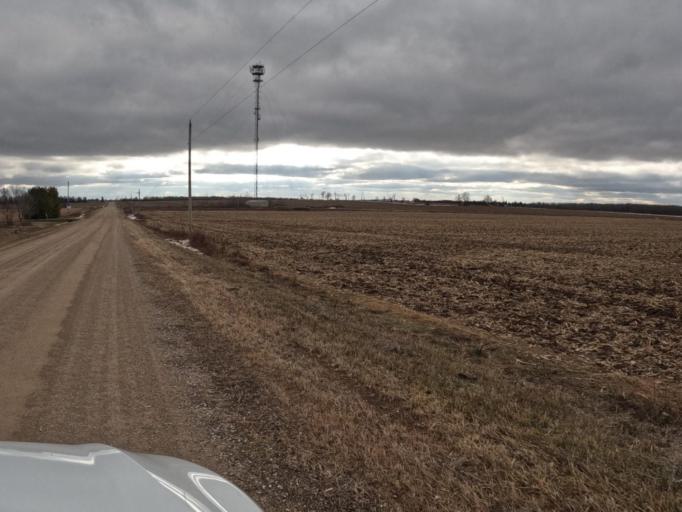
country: CA
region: Ontario
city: Shelburne
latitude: 43.8707
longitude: -80.3786
